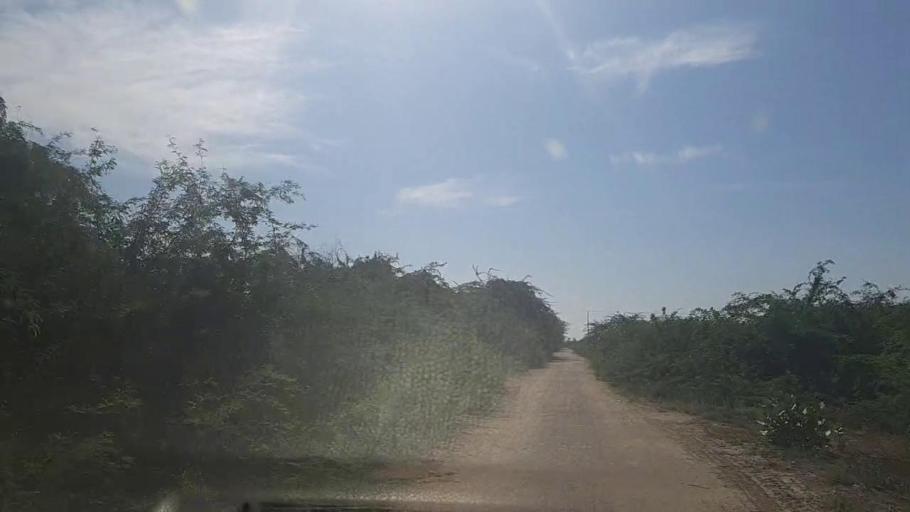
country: PK
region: Sindh
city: Mirpur Batoro
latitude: 24.6741
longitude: 68.1829
